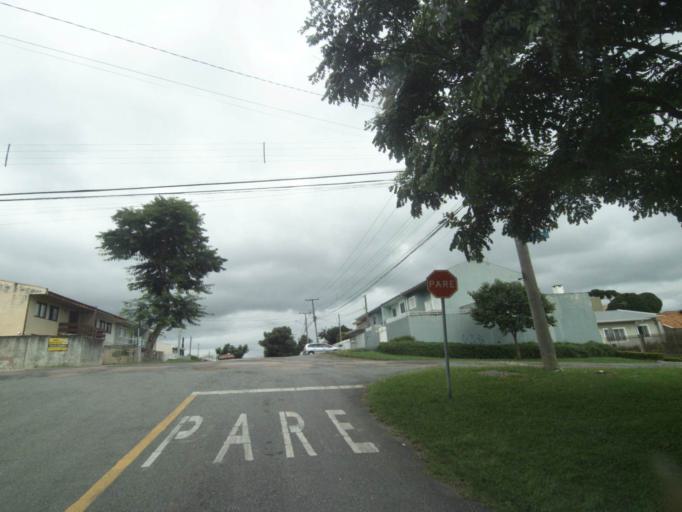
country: BR
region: Parana
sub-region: Curitiba
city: Curitiba
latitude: -25.4901
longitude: -49.2813
